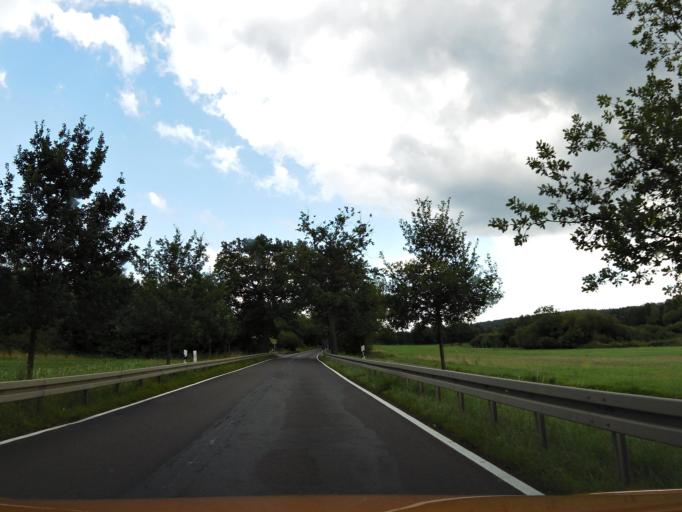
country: DE
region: Brandenburg
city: Potsdam
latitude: 52.4619
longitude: 13.0310
